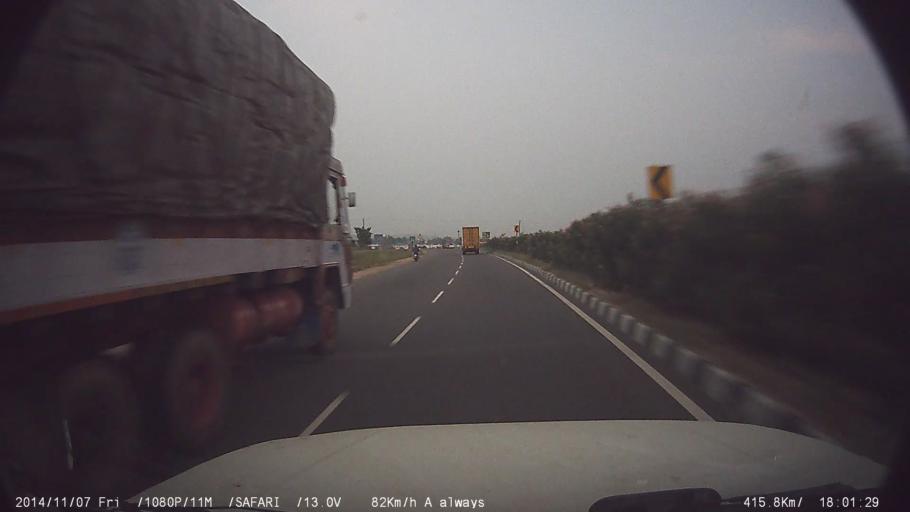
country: IN
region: Tamil Nadu
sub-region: Erode
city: Bhavani
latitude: 11.3798
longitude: 77.6537
